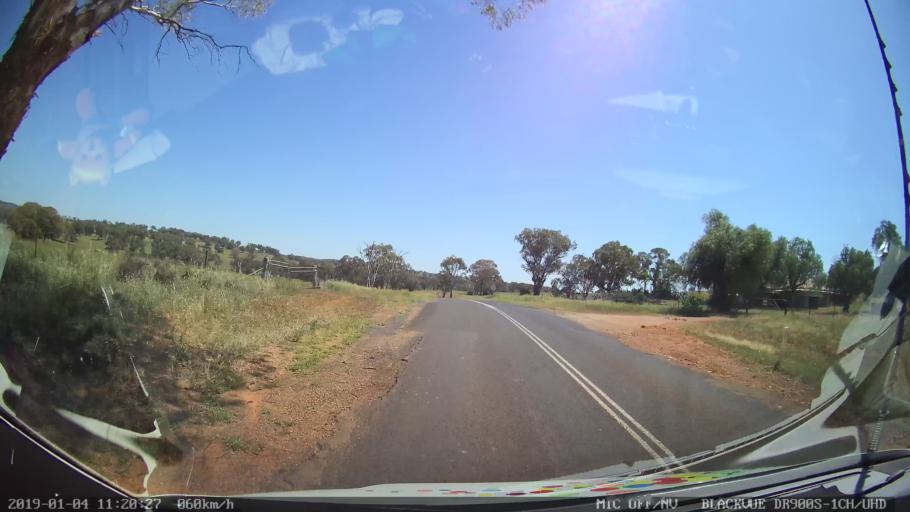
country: AU
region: New South Wales
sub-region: Cabonne
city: Molong
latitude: -33.1636
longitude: 148.7066
